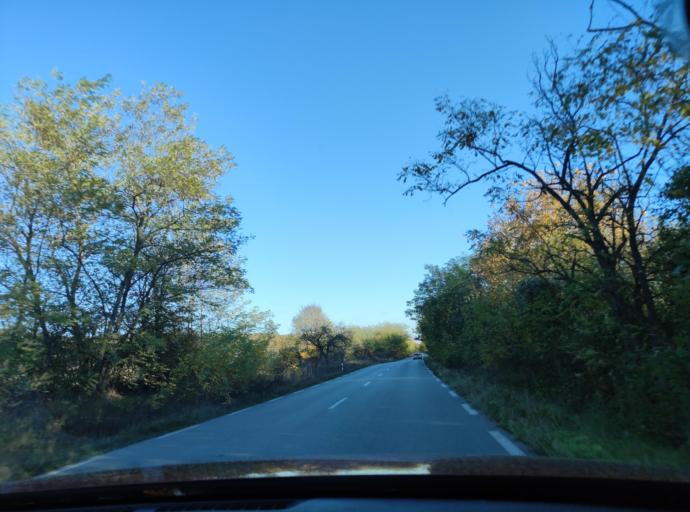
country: BG
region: Montana
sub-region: Obshtina Chiprovtsi
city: Chiprovtsi
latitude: 43.4271
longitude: 23.0051
